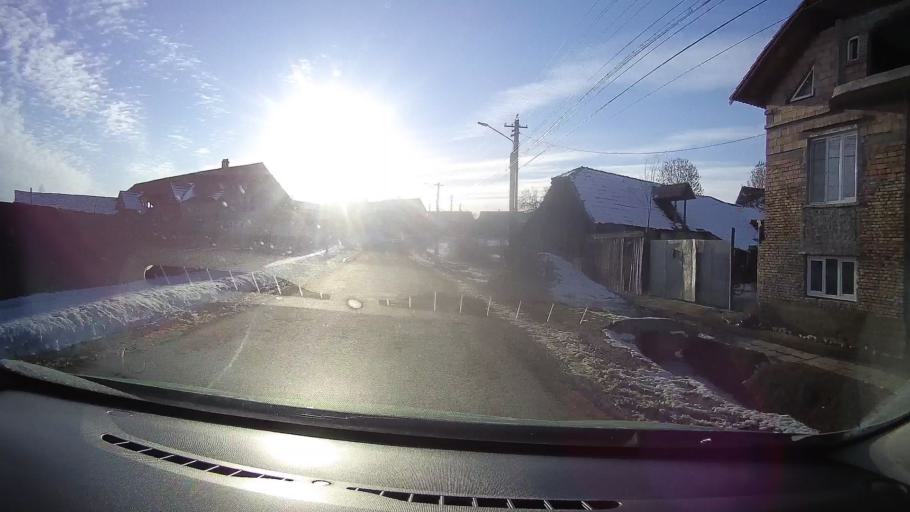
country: RO
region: Sibiu
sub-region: Comuna Merghindeal
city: Merghindeal
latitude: 45.9667
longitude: 24.7198
